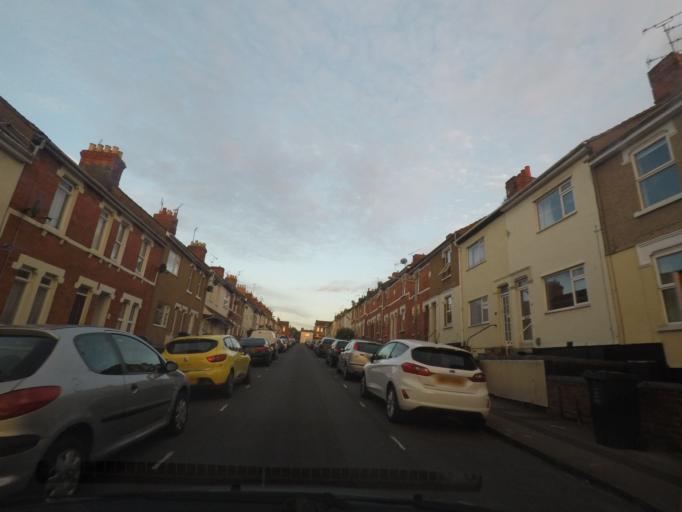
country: GB
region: England
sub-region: Borough of Swindon
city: Swindon
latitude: 51.5577
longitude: -1.7902
